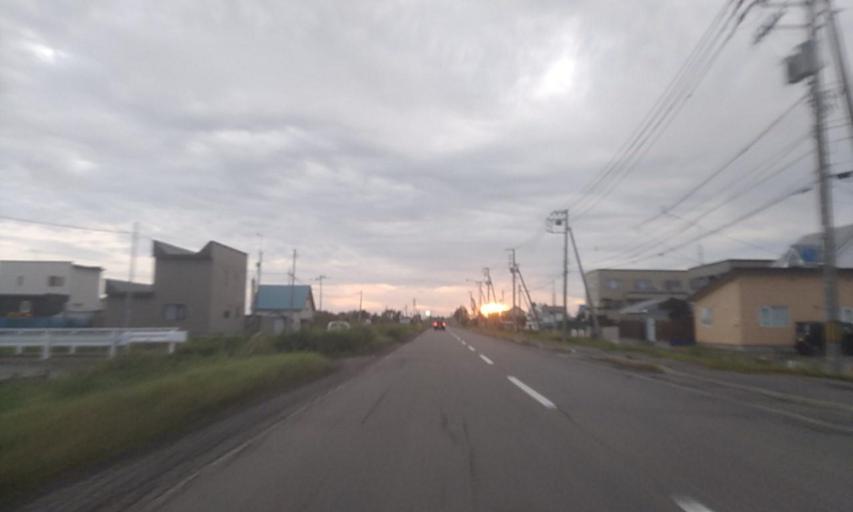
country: JP
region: Hokkaido
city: Abashiri
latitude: 43.9013
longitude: 144.6738
